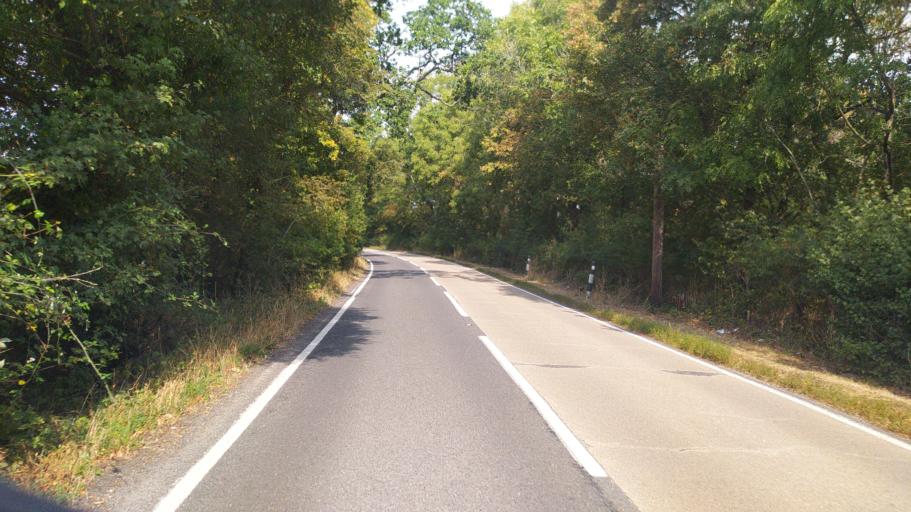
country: GB
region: England
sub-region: Hampshire
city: Havant
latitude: 50.8778
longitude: -0.9590
